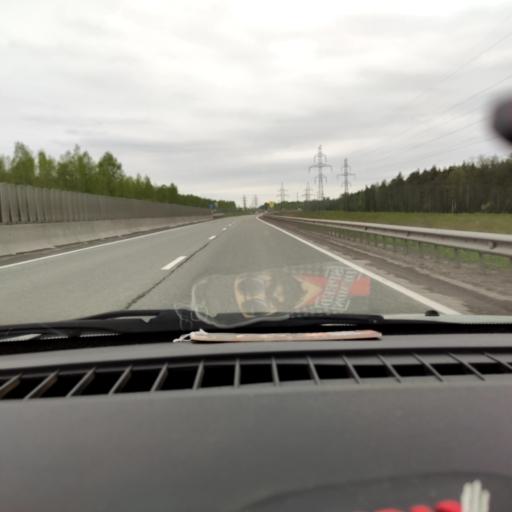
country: RU
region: Perm
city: Overyata
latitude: 58.0365
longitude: 55.9358
